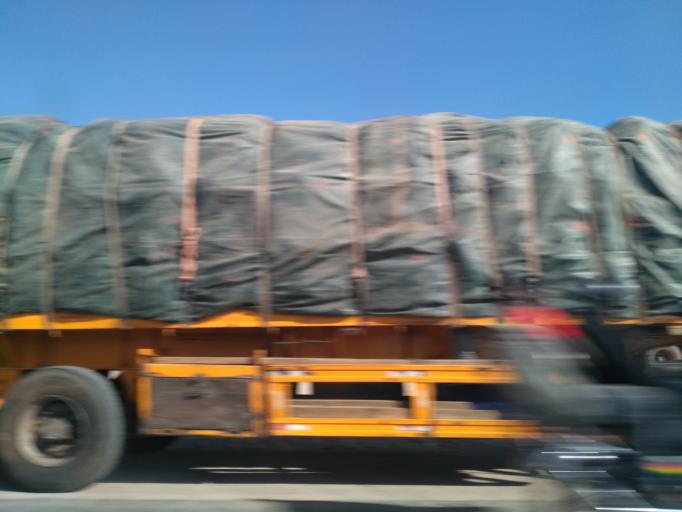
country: TZ
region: Dodoma
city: Dodoma
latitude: -6.1764
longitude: 35.7376
